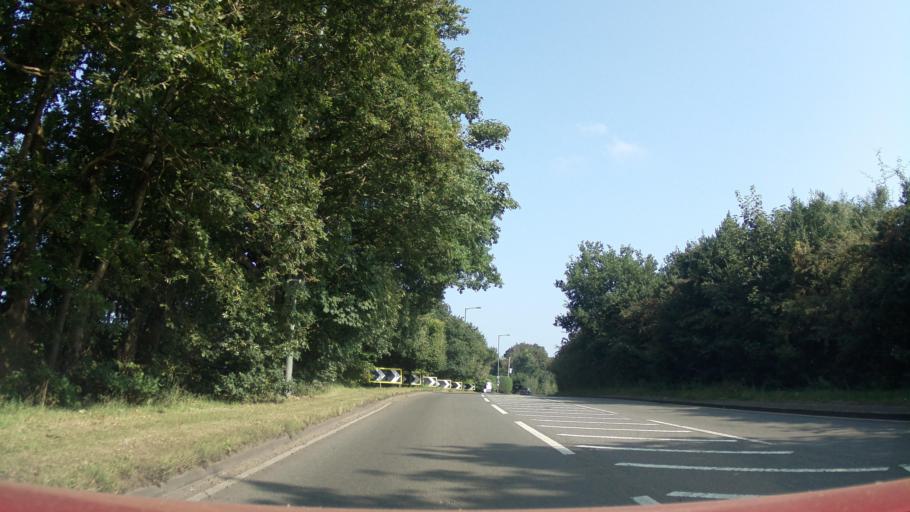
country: GB
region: England
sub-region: Walsall
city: Streetly
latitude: 52.6076
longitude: -1.8871
